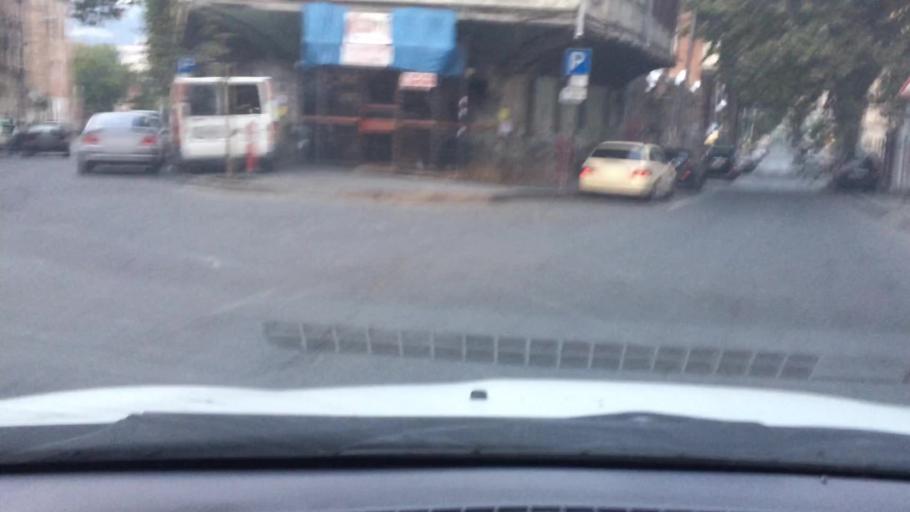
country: GE
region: T'bilisi
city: Tbilisi
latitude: 41.7069
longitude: 44.8024
